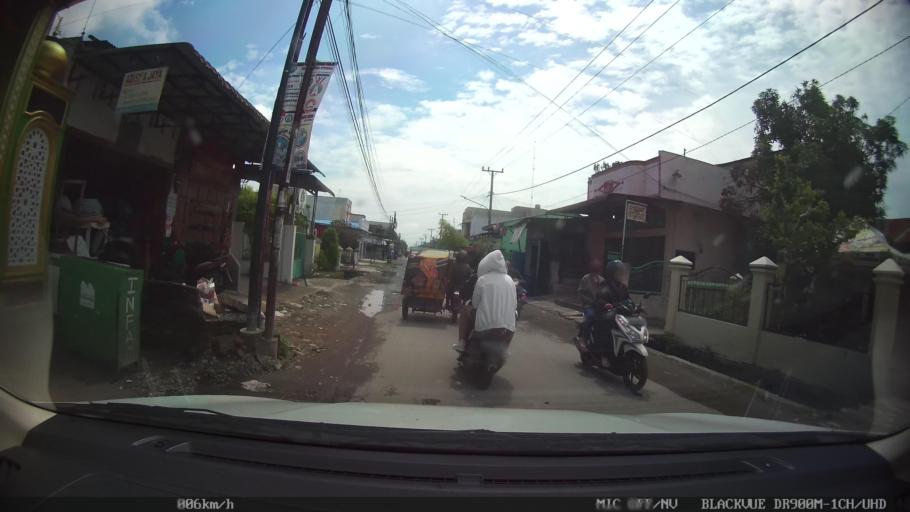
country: ID
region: North Sumatra
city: Medan
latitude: 3.5910
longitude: 98.7525
